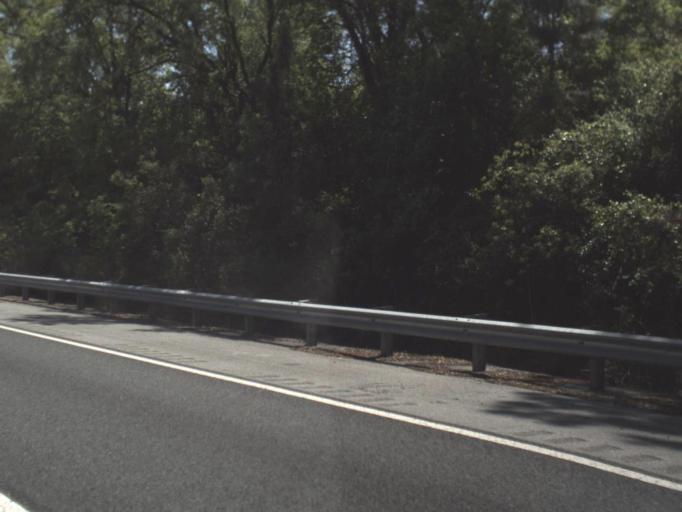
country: US
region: Florida
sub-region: Escambia County
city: Ferry Pass
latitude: 30.5036
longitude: -87.2405
